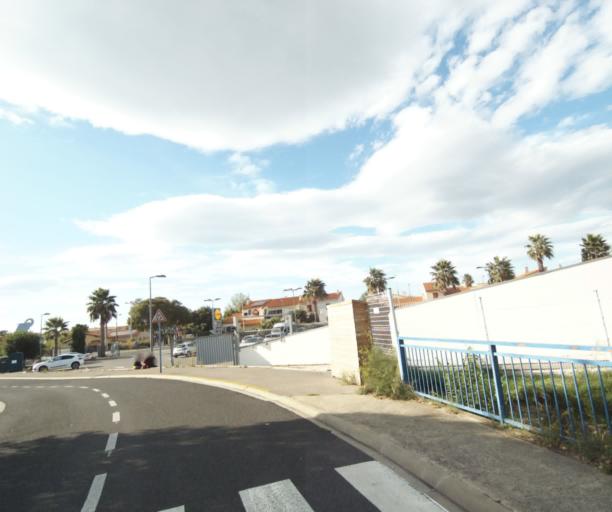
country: FR
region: Languedoc-Roussillon
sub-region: Departement des Pyrenees-Orientales
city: Argelers
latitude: 42.5454
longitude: 3.0306
